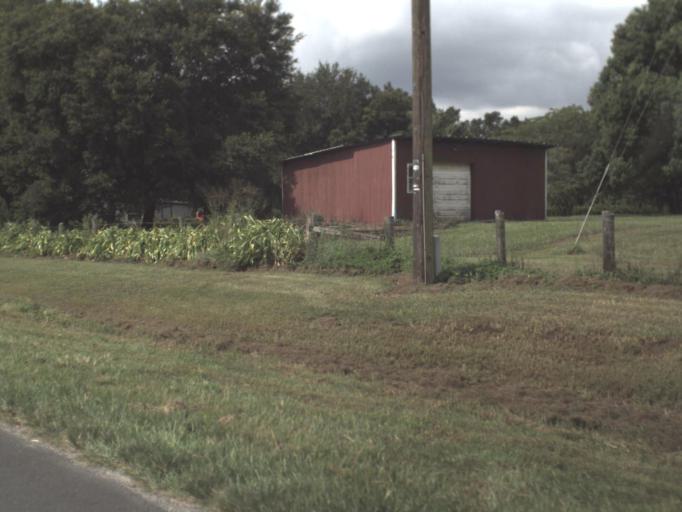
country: US
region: Florida
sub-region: Hillsborough County
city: Plant City
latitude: 28.0936
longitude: -82.1412
